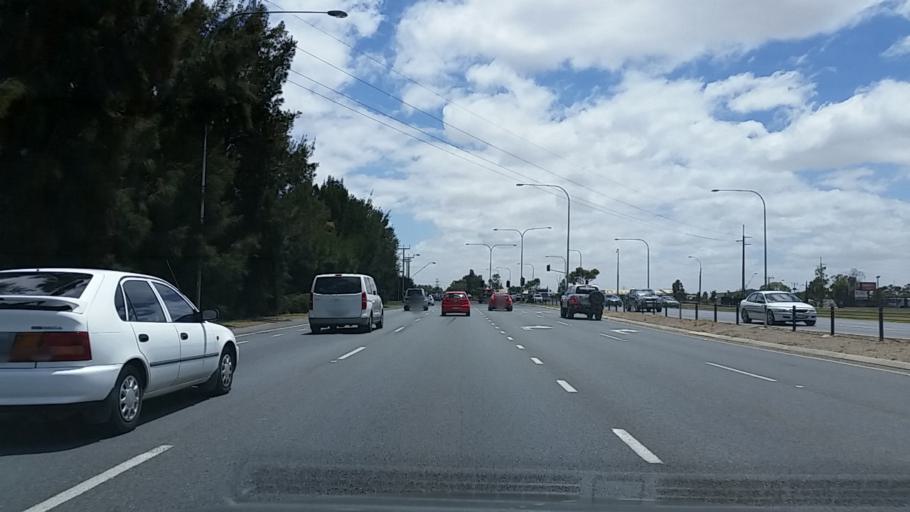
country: AU
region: South Australia
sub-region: Salisbury
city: Salisbury
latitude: -34.7956
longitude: 138.5965
